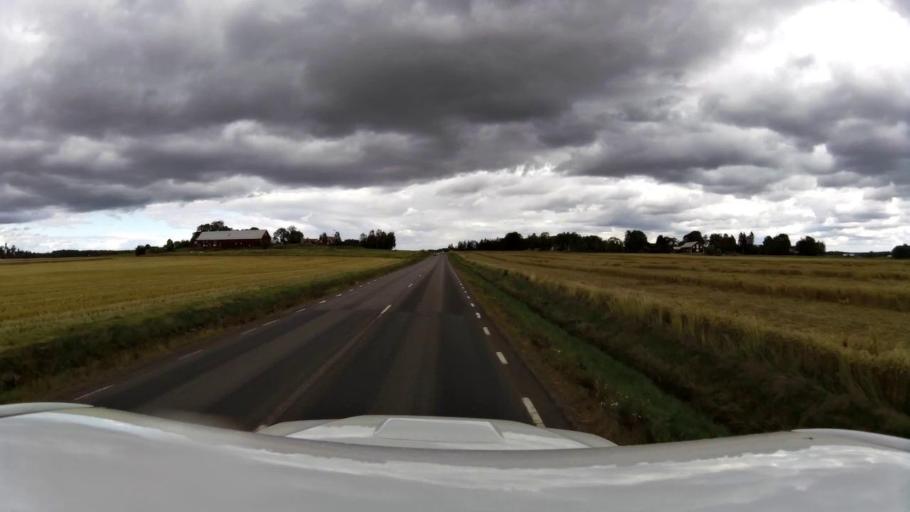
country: SE
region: OEstergoetland
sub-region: Linkopings Kommun
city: Linghem
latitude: 58.3926
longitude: 15.7568
